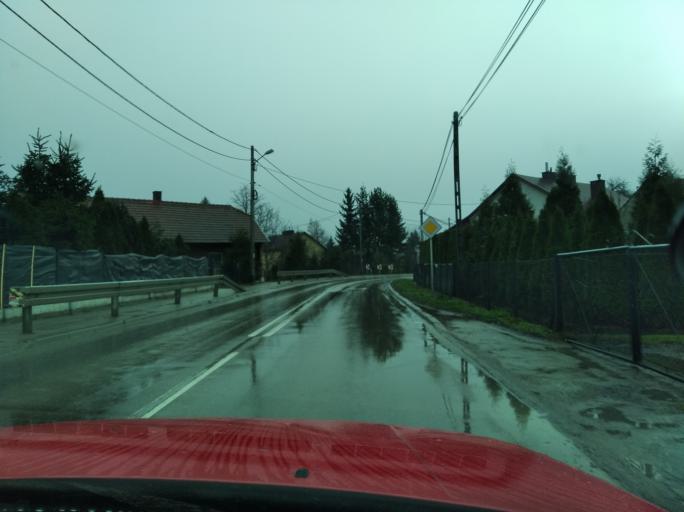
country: PL
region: Subcarpathian Voivodeship
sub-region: Rzeszow
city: Rzeszow
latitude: 50.0004
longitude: 21.9913
